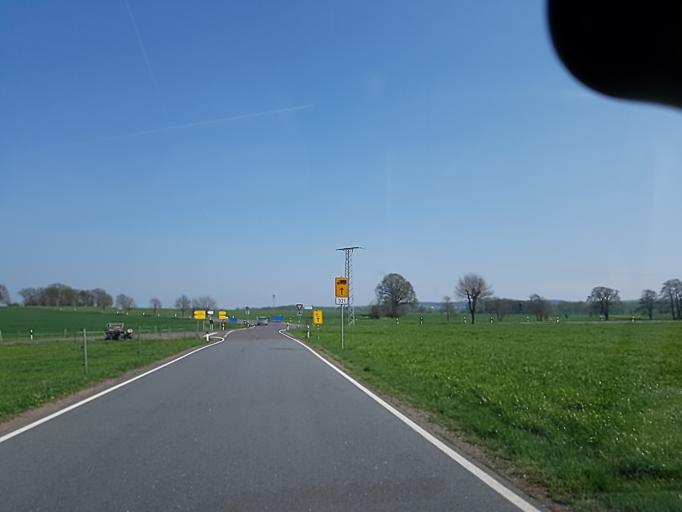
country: DE
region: Saxony
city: Cavertitz
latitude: 51.3885
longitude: 13.0963
